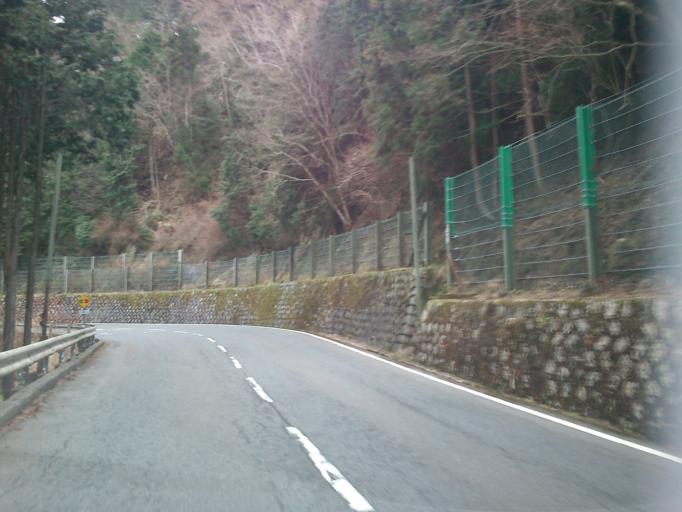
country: JP
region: Shiga Prefecture
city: Otsu-shi
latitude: 35.0672
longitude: 135.8413
